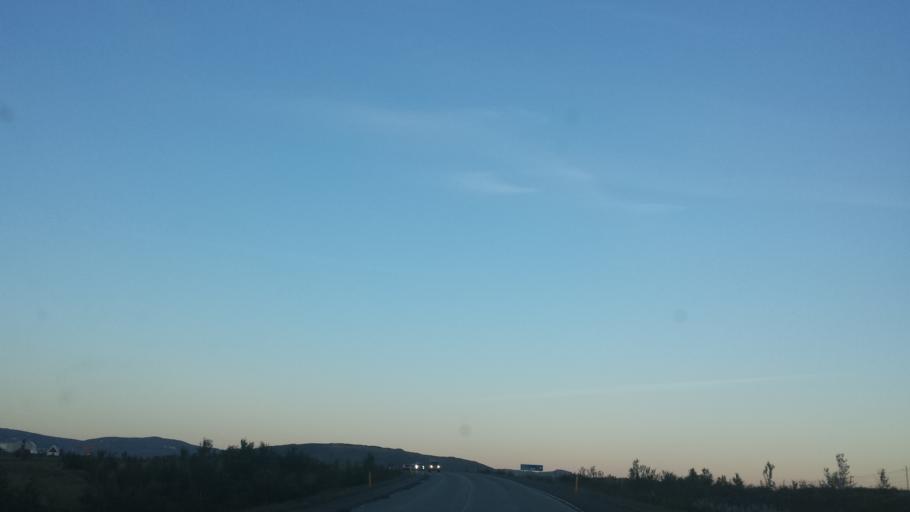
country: IS
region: Capital Region
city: Mosfellsbaer
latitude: 64.1980
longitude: -21.7062
